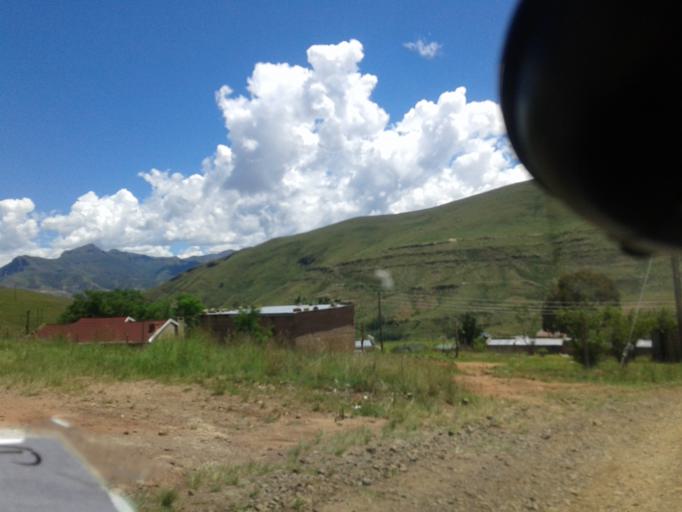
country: LS
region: Qacha's Nek
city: Qacha's Nek
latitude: -30.0919
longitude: 28.6418
